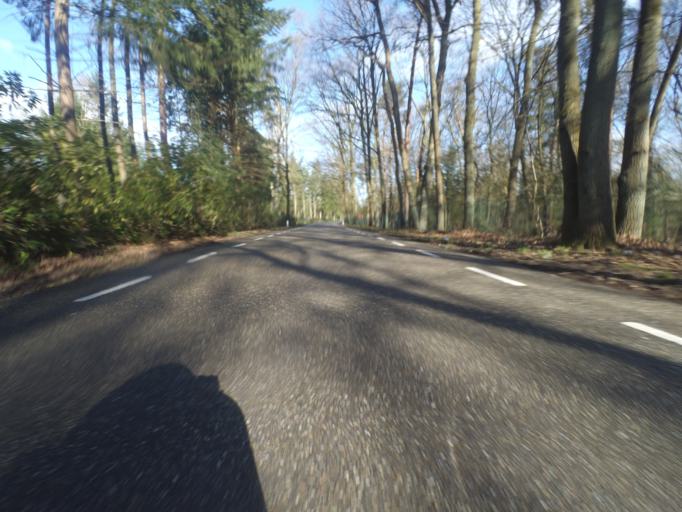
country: NL
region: Gelderland
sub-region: Gemeente Apeldoorn
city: Beekbergen
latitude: 52.1775
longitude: 5.9334
